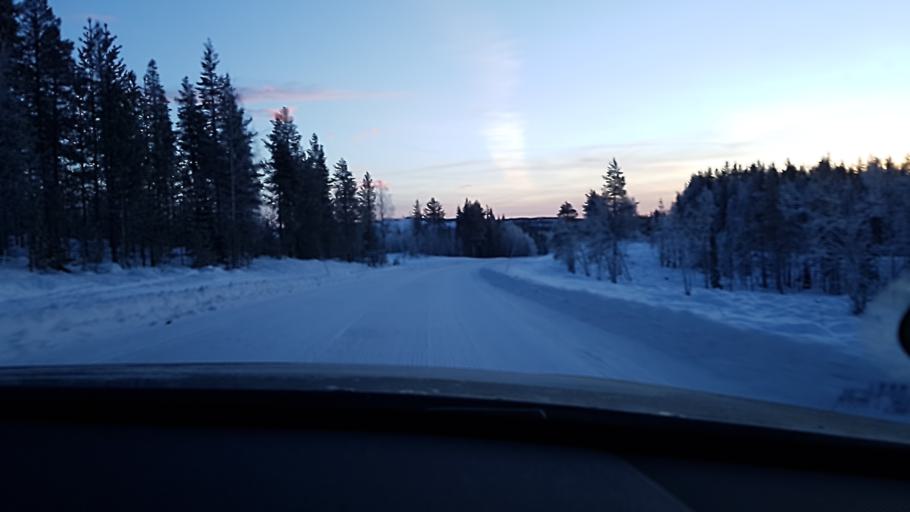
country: SE
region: Vaesterbotten
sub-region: Storumans Kommun
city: Storuman
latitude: 65.1477
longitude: 17.2608
